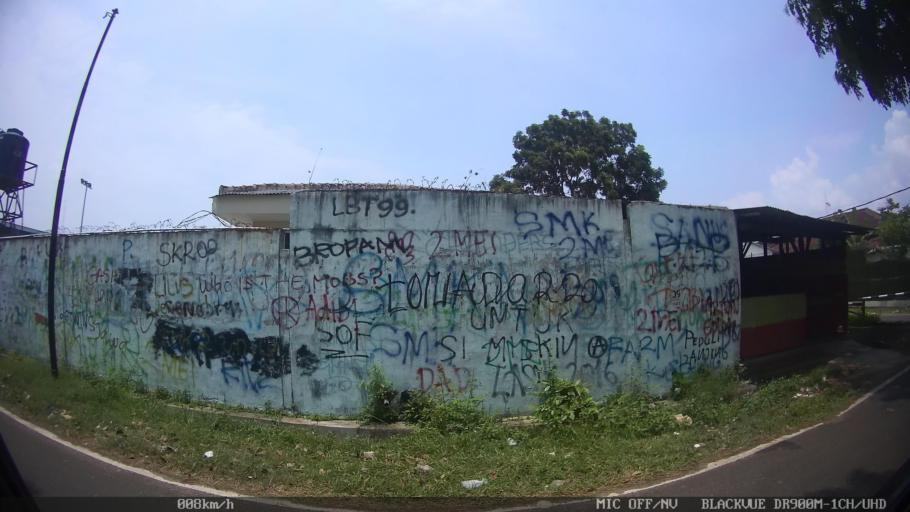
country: ID
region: Lampung
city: Bandarlampung
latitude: -5.4261
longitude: 105.2681
